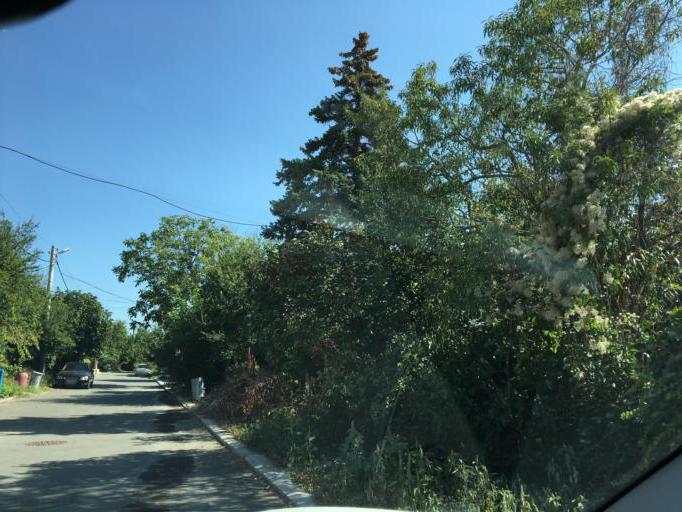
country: BG
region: Burgas
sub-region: Obshtina Kameno
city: Kameno
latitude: 42.6103
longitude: 27.3873
